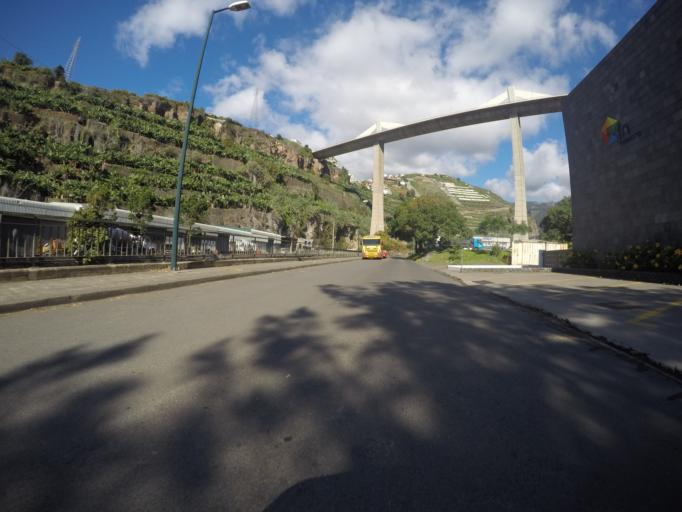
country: PT
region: Madeira
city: Camara de Lobos
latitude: 32.6528
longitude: -16.9646
